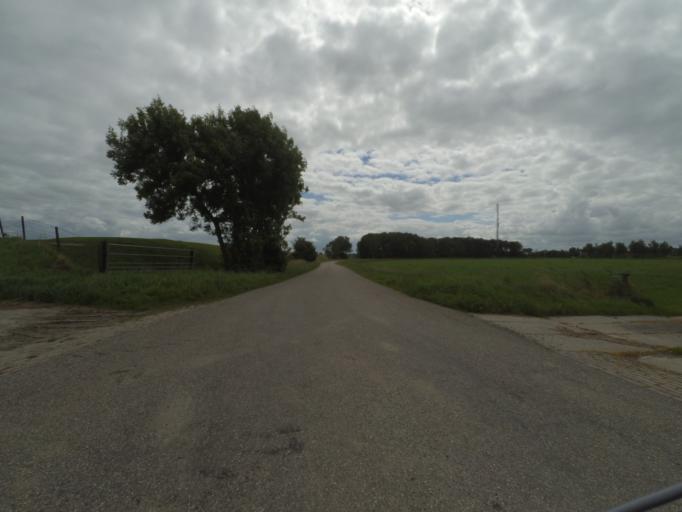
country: NL
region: Friesland
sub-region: Gemeente Kollumerland en Nieuwkruisland
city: Kollum
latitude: 53.3276
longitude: 6.1548
